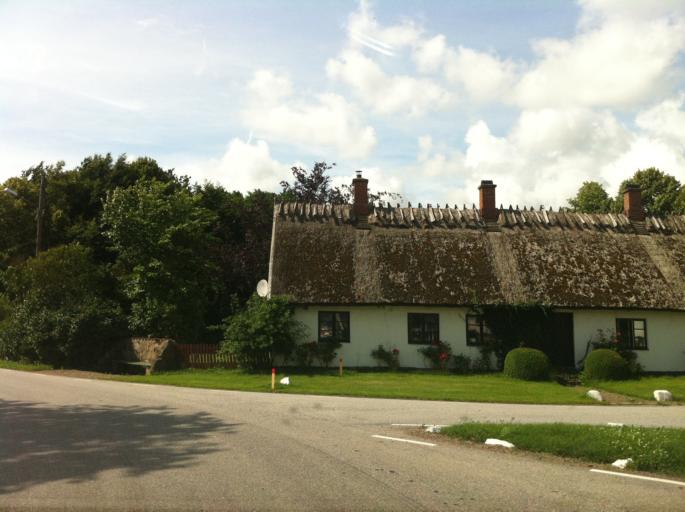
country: SE
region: Skane
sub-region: Trelleborgs Kommun
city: Anderslov
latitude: 55.5006
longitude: 13.3903
